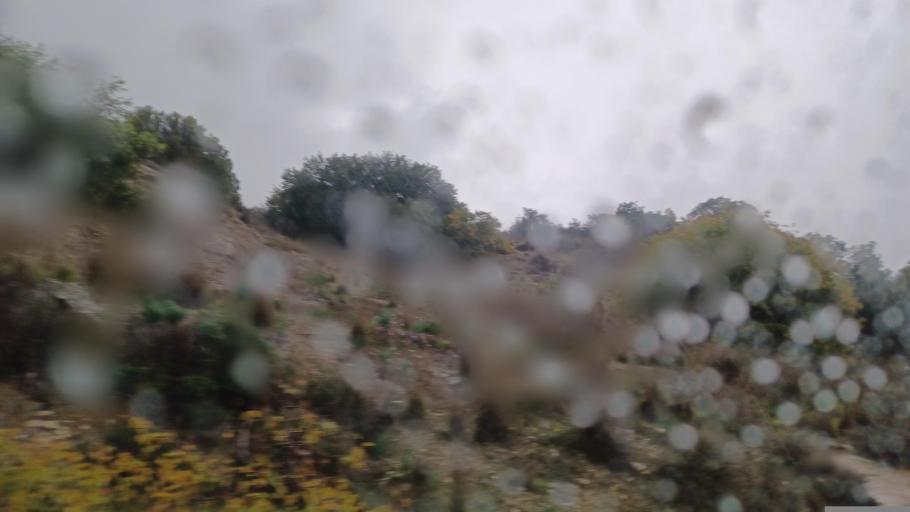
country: CY
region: Pafos
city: Mesogi
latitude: 34.8730
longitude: 32.5408
